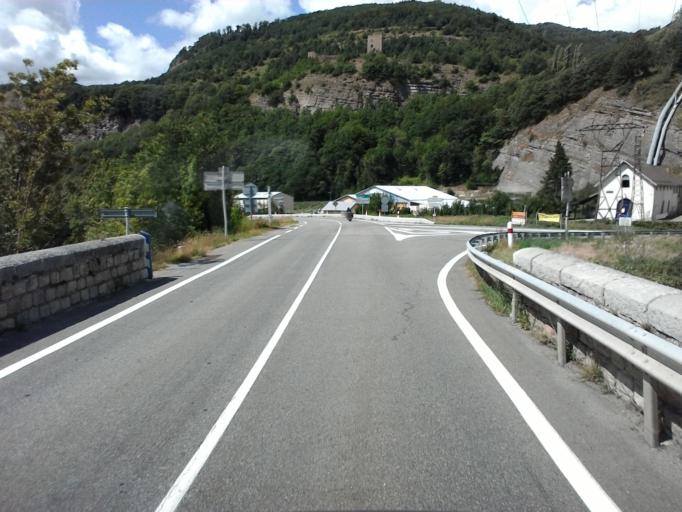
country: FR
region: Provence-Alpes-Cote d'Azur
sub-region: Departement des Hautes-Alpes
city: Saint-Bonnet-en-Champsaur
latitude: 44.7743
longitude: 6.0178
